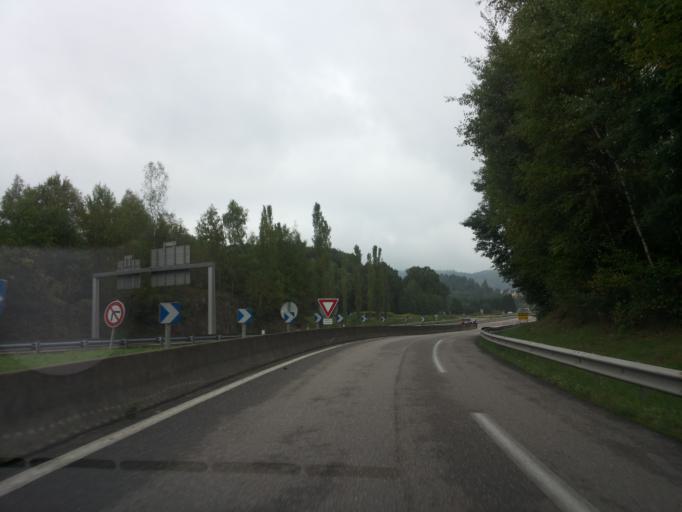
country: FR
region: Lorraine
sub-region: Departement des Vosges
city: Remiremont
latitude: 48.0332
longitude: 6.5809
